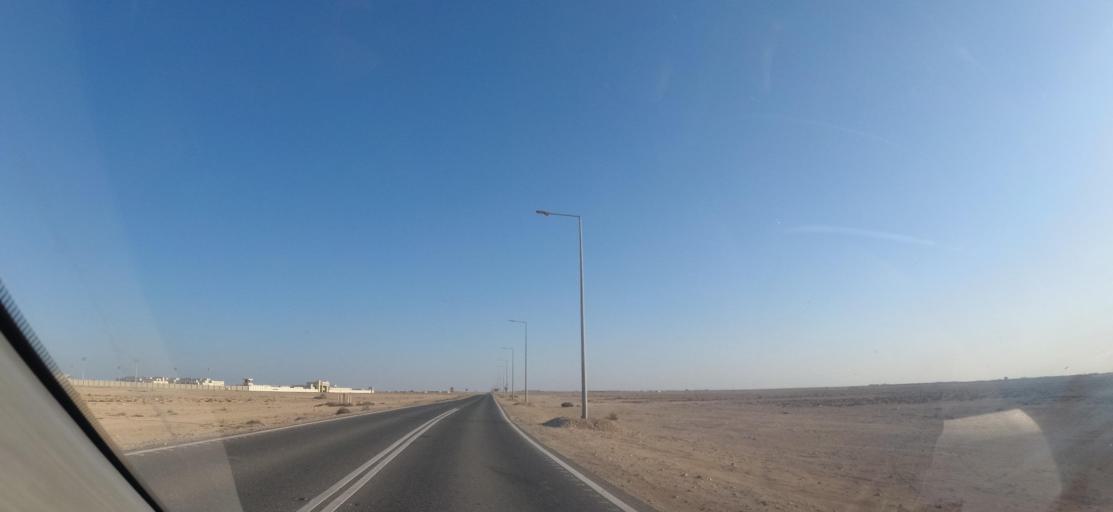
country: QA
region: Madinat ash Shamal
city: Ar Ru'ays
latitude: 26.1318
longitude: 51.2316
